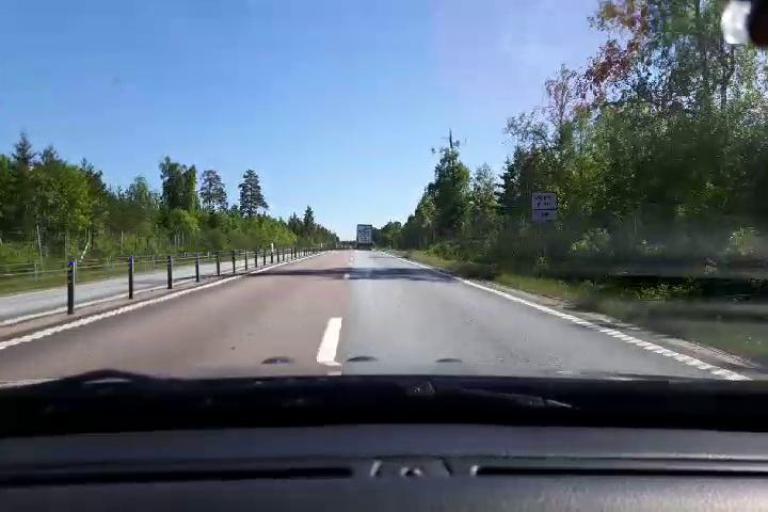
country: SE
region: Gaevleborg
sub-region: Soderhamns Kommun
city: Soderhamn
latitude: 61.2677
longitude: 17.0285
